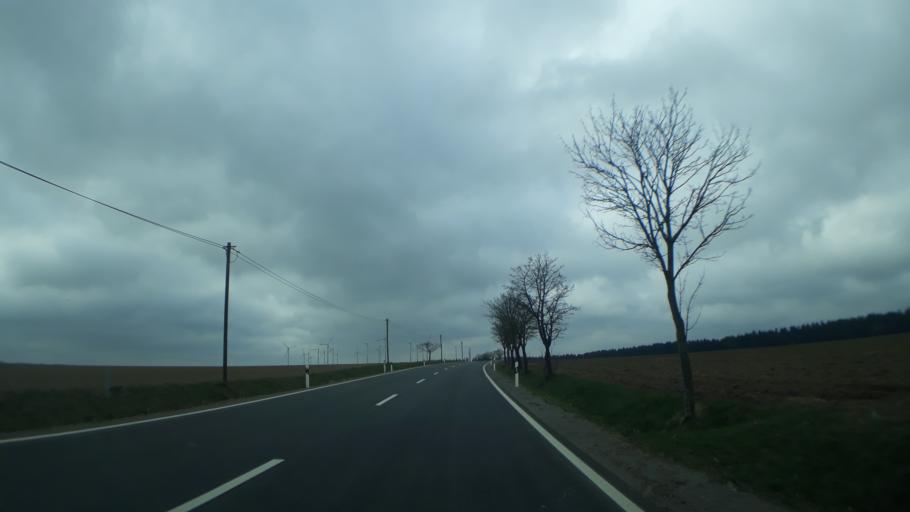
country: DE
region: North Rhine-Westphalia
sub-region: Regierungsbezirk Koln
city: Hellenthal
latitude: 50.5377
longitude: 6.3980
